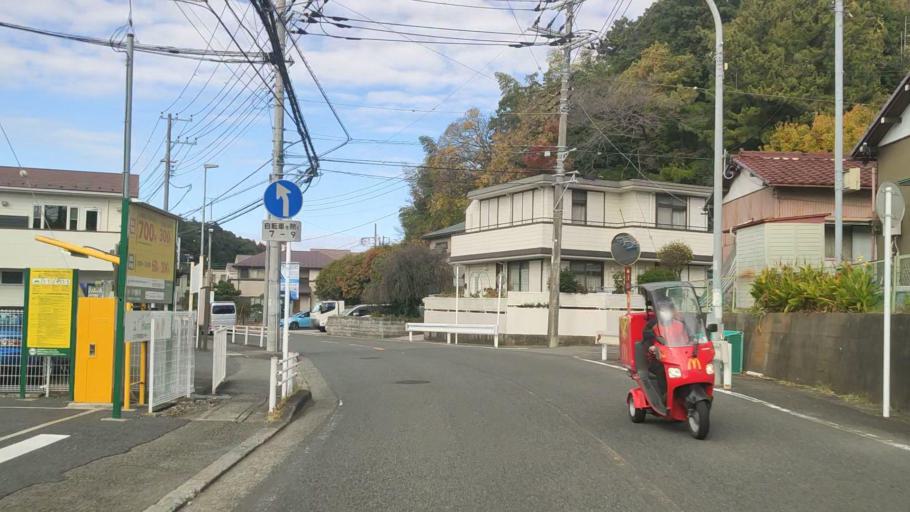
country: JP
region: Kanagawa
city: Yokohama
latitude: 35.4339
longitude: 139.5480
